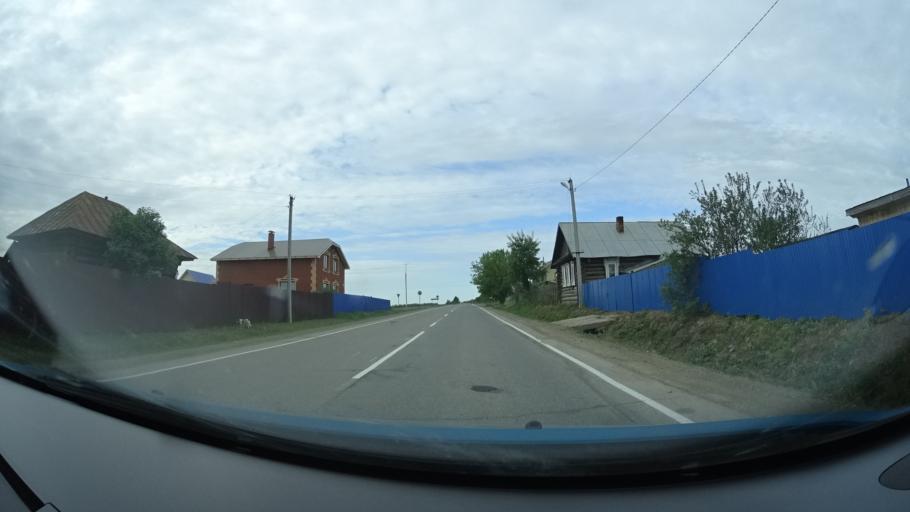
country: RU
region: Perm
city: Barda
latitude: 56.8816
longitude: 55.6003
